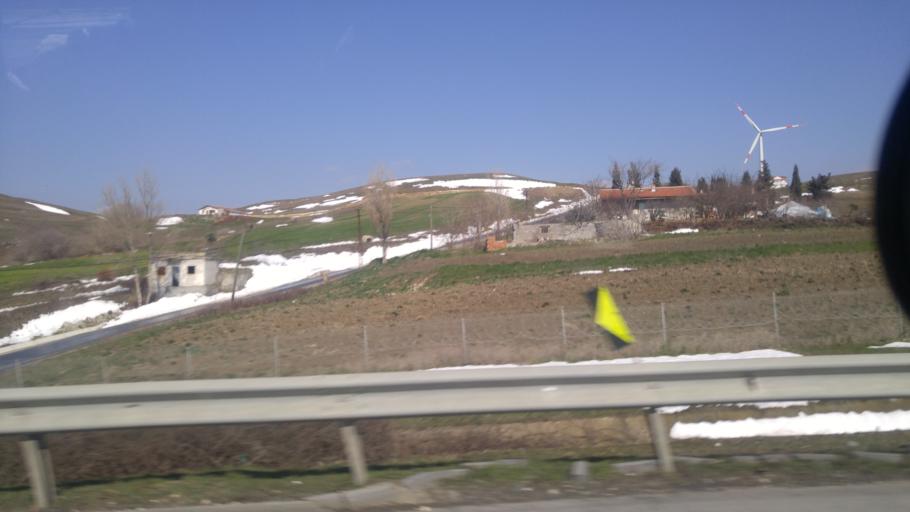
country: TR
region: Istanbul
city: Celaliye
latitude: 41.0518
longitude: 28.4346
